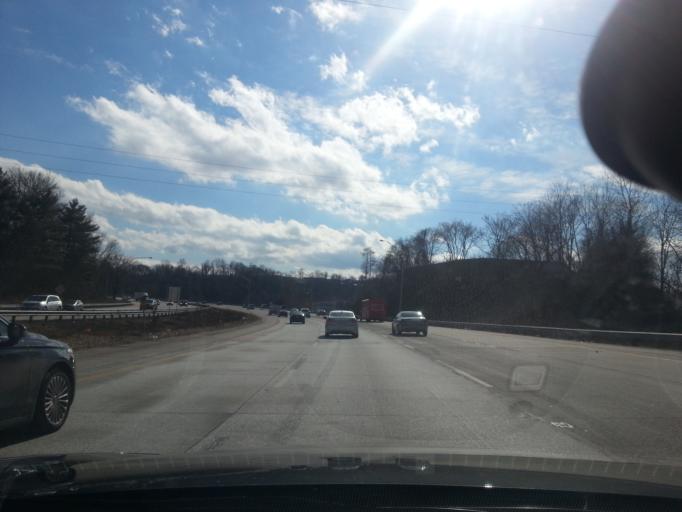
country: US
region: Pennsylvania
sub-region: Montgomery County
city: West Conshohocken
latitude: 40.0759
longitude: -75.3215
